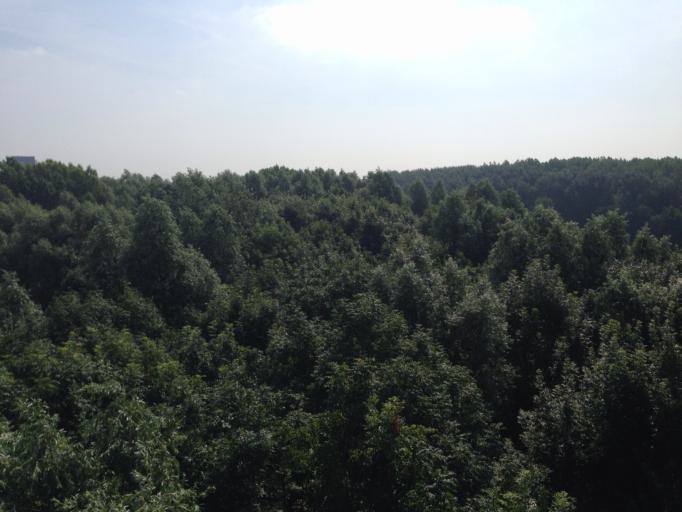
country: NL
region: Flevoland
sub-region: Gemeente Almere
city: Almere Stad
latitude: 52.3605
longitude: 5.2256
